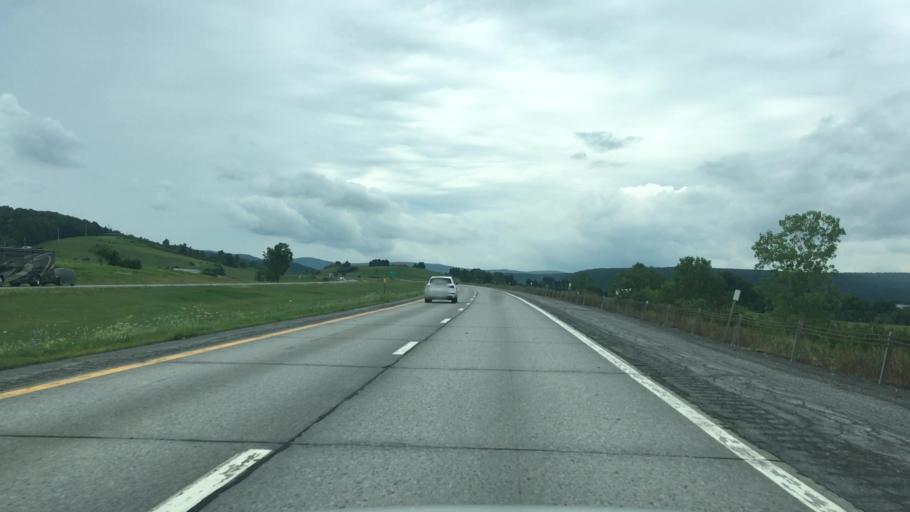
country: US
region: New York
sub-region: Schoharie County
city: Cobleskill
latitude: 42.6713
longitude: -74.4828
